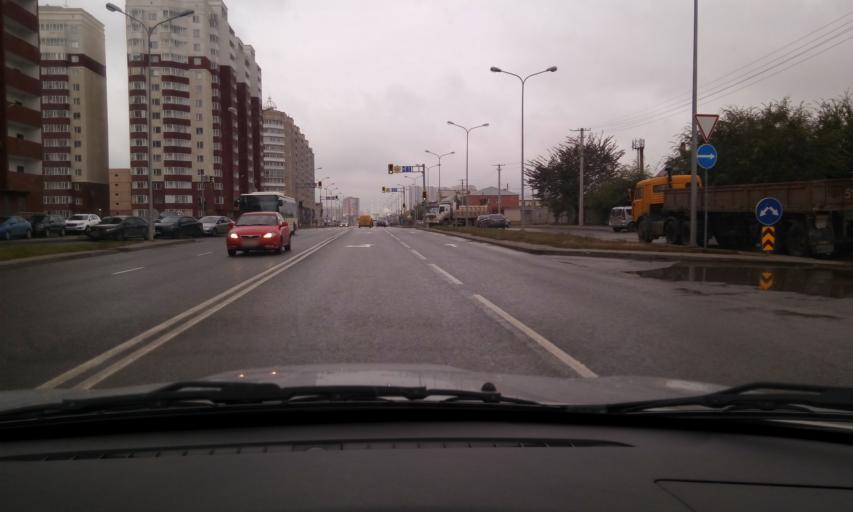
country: KZ
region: Astana Qalasy
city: Astana
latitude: 51.1331
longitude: 71.5015
